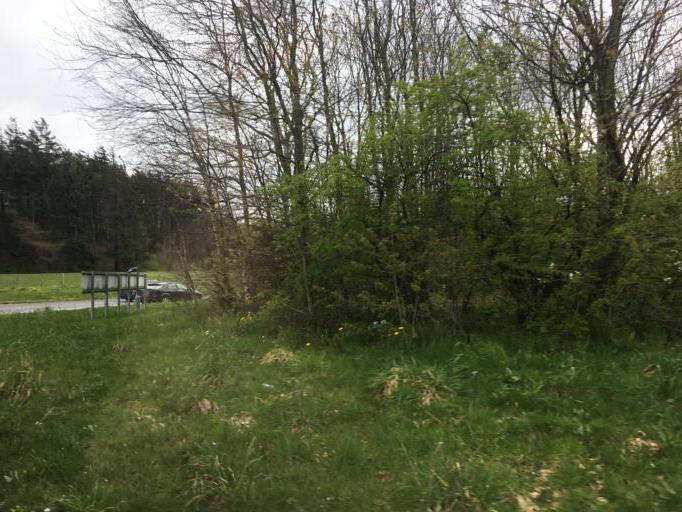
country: GB
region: Wales
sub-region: Gwynedd
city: Y Felinheli
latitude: 53.1682
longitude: -4.2373
